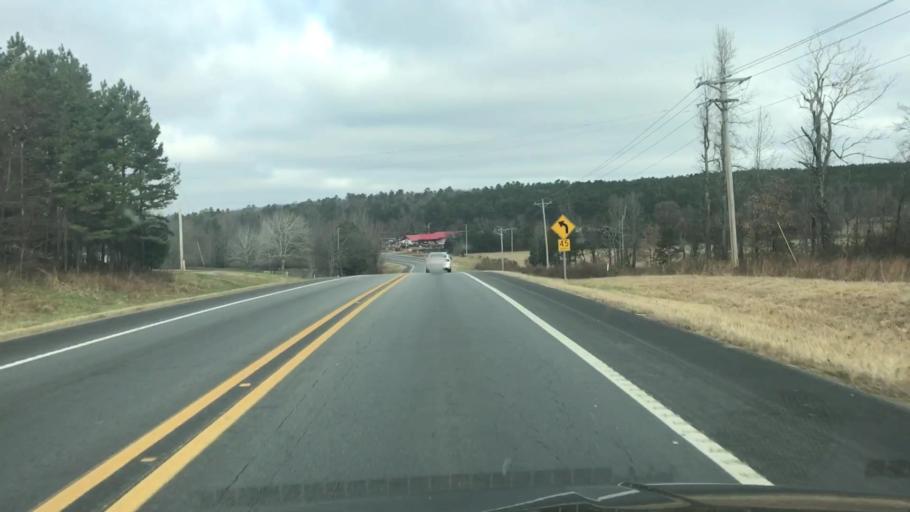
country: US
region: Arkansas
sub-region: Scott County
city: Waldron
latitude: 34.8346
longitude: -94.0440
